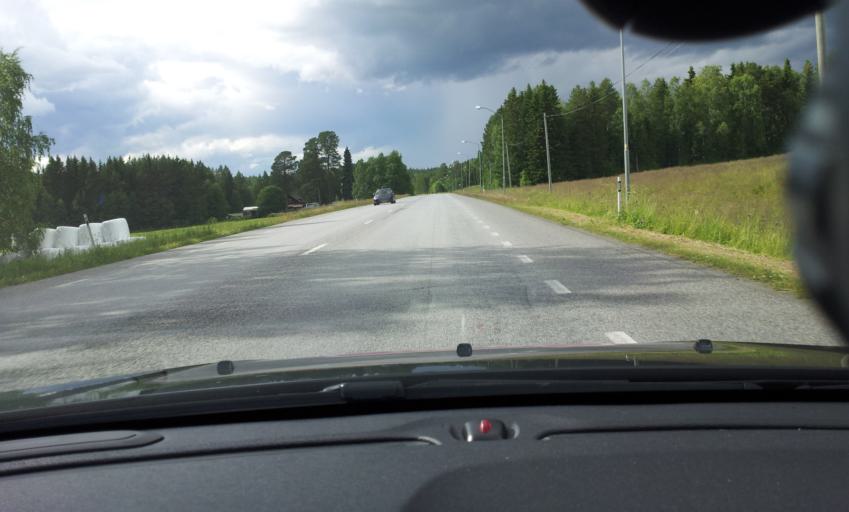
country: SE
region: Jaemtland
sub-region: Are Kommun
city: Jarpen
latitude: 63.3321
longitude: 13.5231
